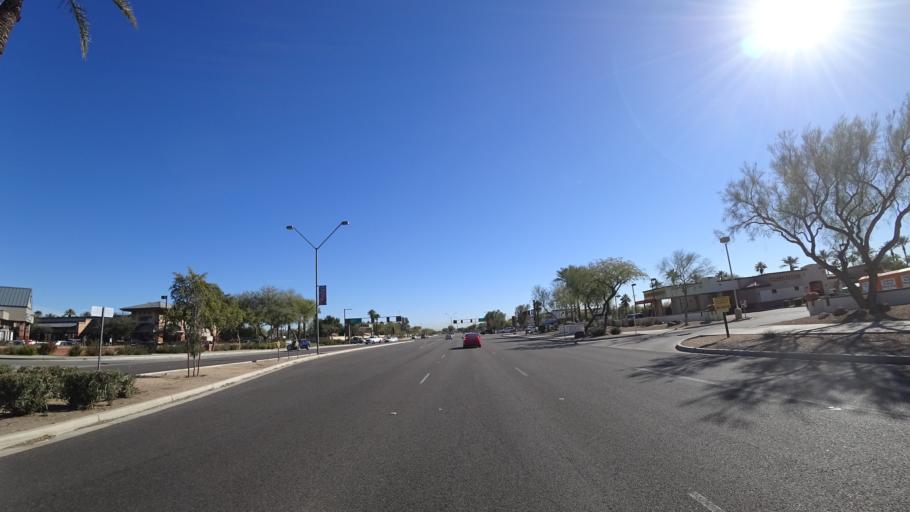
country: US
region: Arizona
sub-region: Maricopa County
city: Litchfield Park
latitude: 33.4857
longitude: -112.3640
